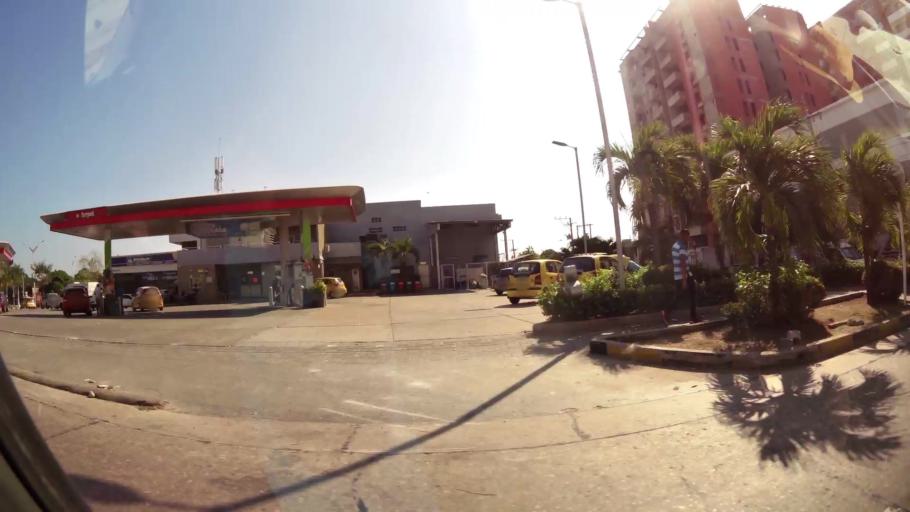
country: CO
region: Atlantico
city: Barranquilla
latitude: 10.9921
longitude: -74.7892
